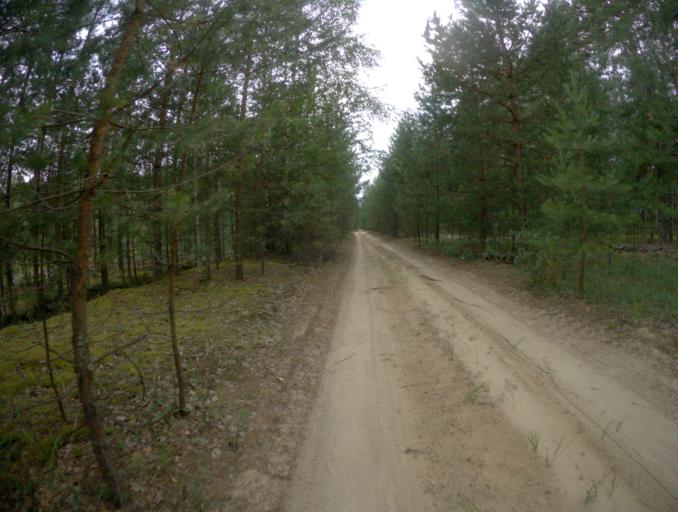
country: RU
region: Nizjnij Novgorod
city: Frolishchi
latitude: 56.4705
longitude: 42.6837
